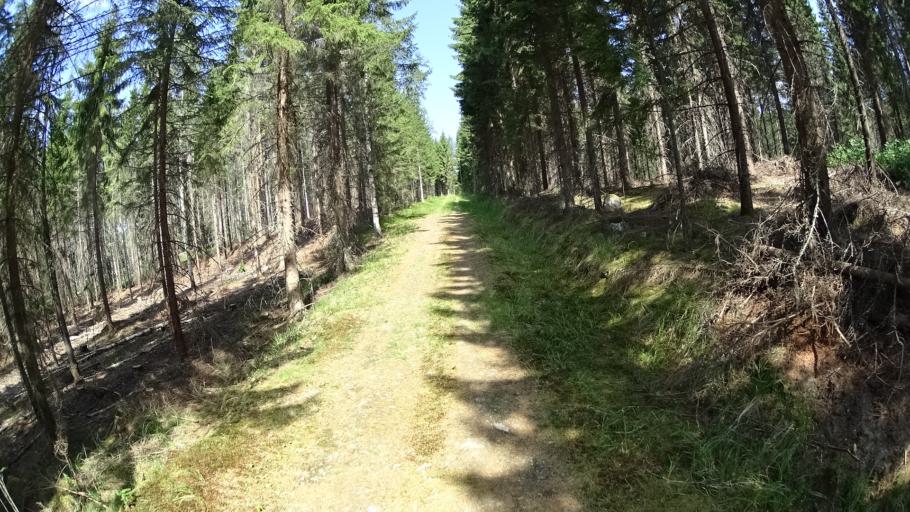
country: FI
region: North Karelia
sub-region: Pielisen Karjala
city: Lieksa
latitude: 63.1266
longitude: 29.7991
